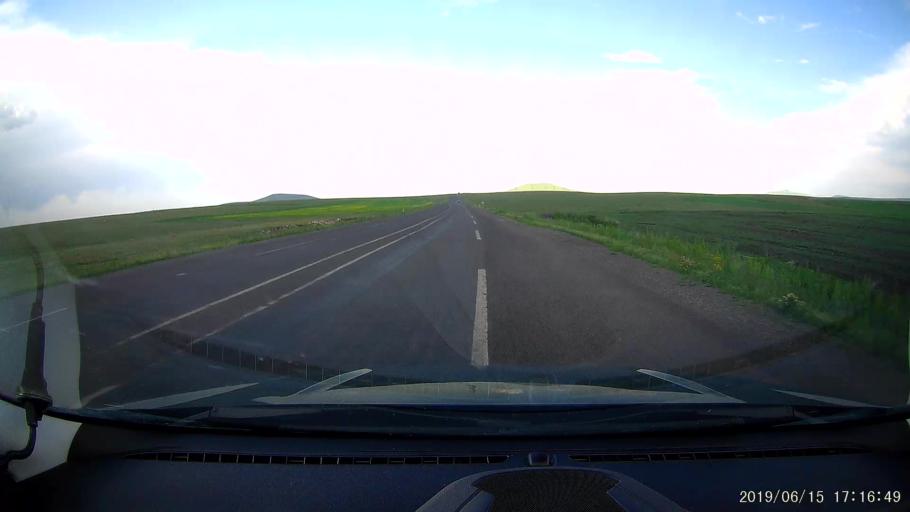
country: TR
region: Kars
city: Kars
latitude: 40.6142
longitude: 43.2253
